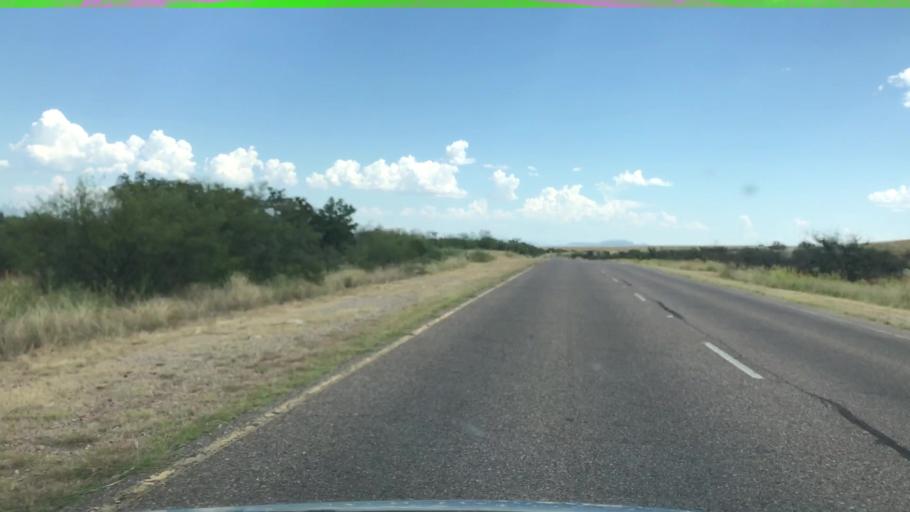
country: US
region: Arizona
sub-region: Cochise County
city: Sierra Vista
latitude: 31.5435
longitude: -110.3315
